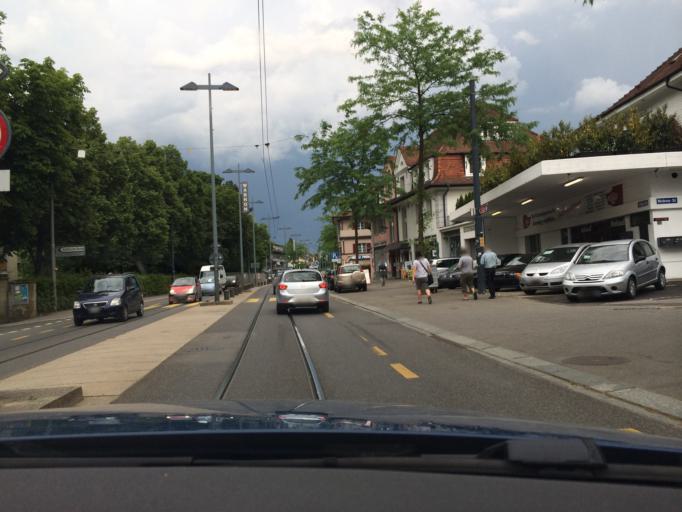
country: CH
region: Bern
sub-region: Bern-Mittelland District
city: Bern
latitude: 46.9296
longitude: 7.4493
